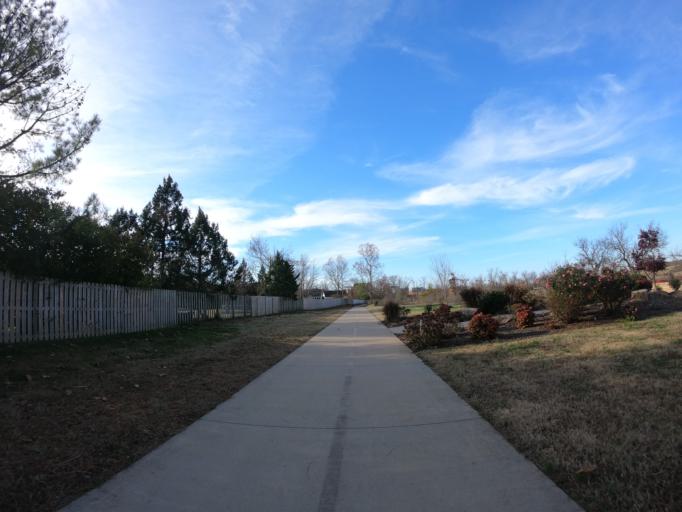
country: US
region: Arkansas
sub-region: Benton County
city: Lowell
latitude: 36.2934
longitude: -94.1756
